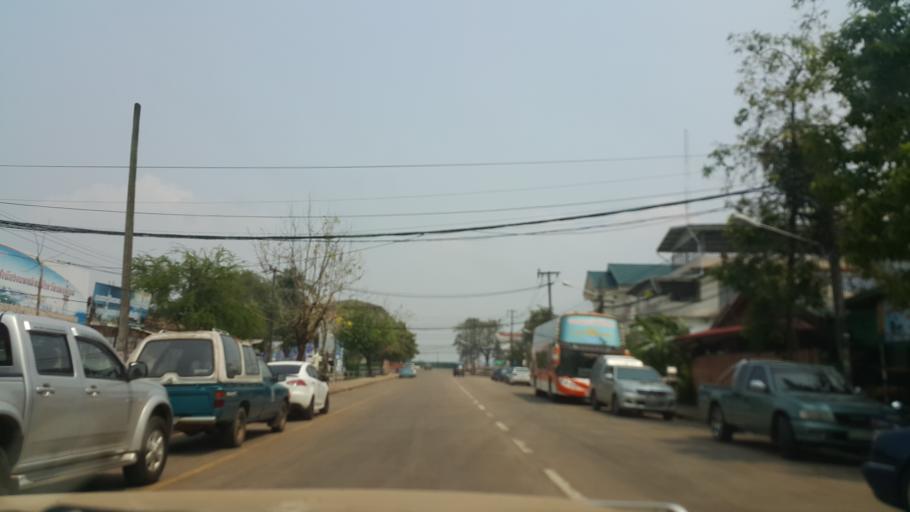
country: TH
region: Nakhon Phanom
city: Nakhon Phanom
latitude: 17.4072
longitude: 104.7836
